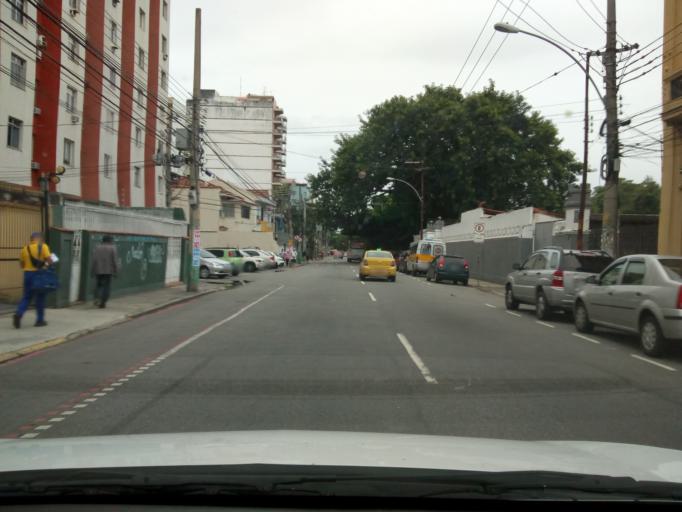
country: BR
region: Rio de Janeiro
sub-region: Rio De Janeiro
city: Rio de Janeiro
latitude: -22.9193
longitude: -43.2307
